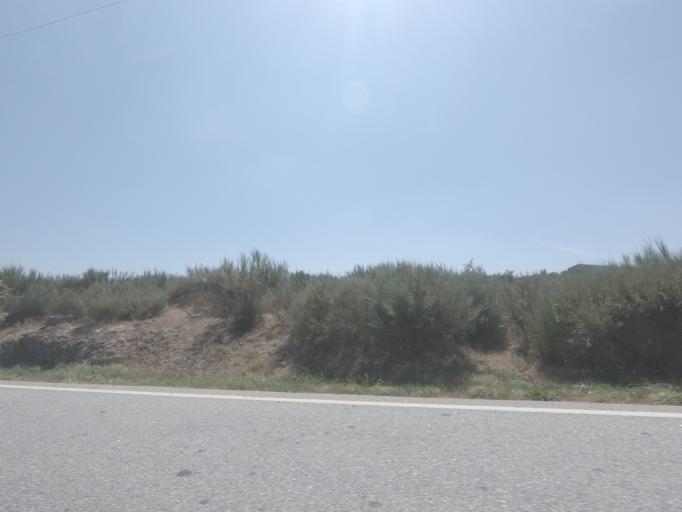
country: PT
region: Viseu
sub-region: Tarouca
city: Tarouca
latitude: 41.0003
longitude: -7.8867
